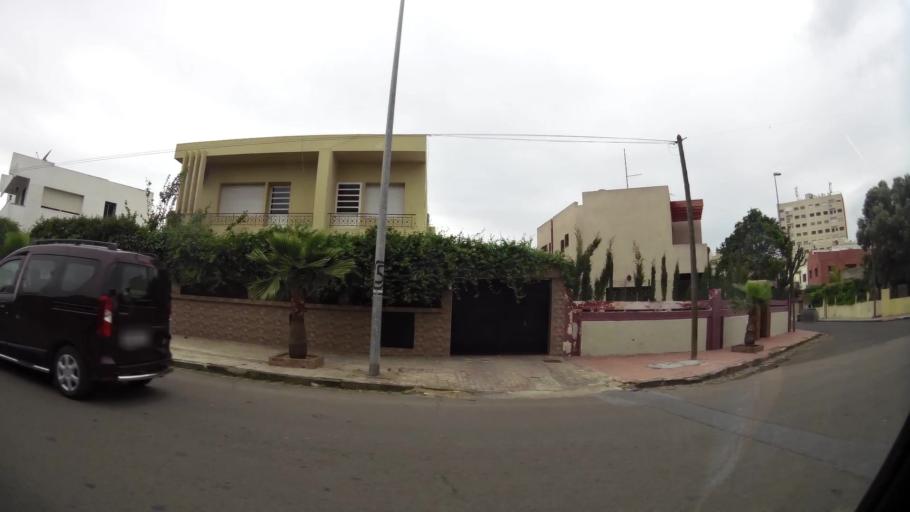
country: MA
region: Grand Casablanca
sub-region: Casablanca
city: Casablanca
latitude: 33.5945
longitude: -7.6477
